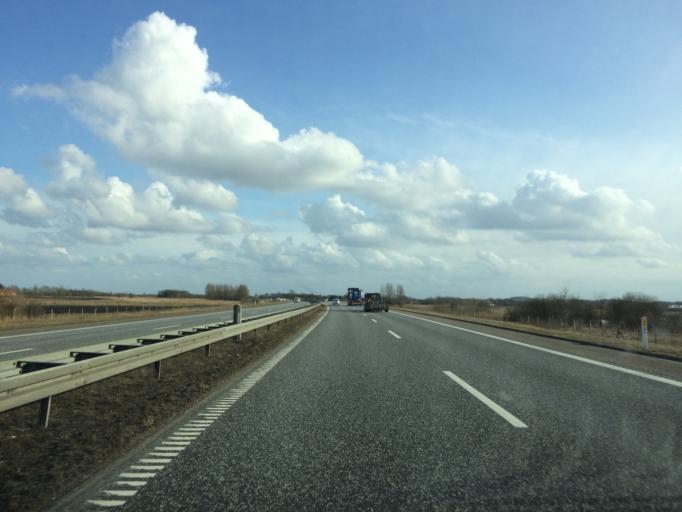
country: DK
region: North Denmark
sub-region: Alborg Kommune
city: Vestbjerg
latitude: 57.1241
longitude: 9.9405
